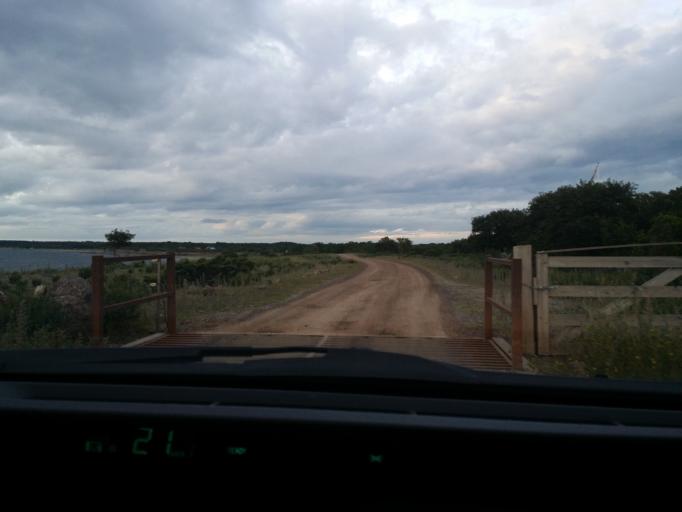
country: SE
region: Kalmar
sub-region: Borgholms Kommun
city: Borgholm
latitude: 57.2046
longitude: 16.9231
